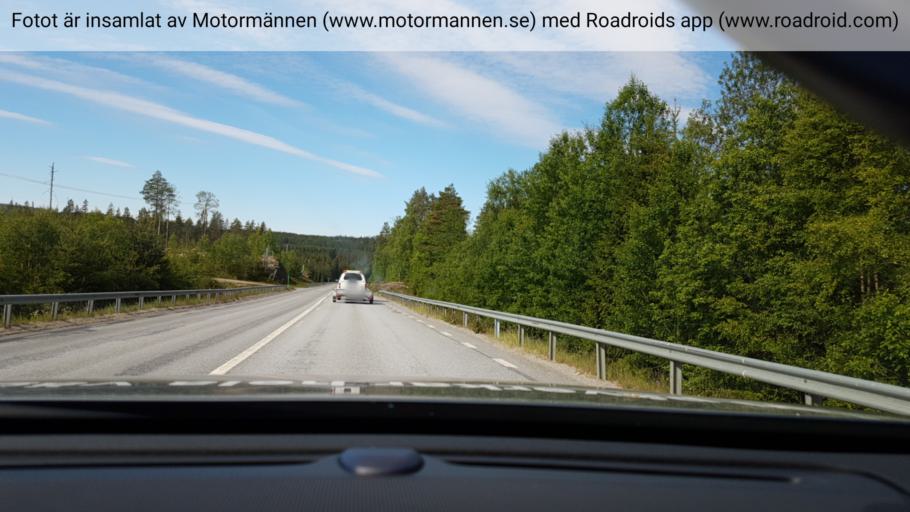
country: SE
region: Vaesterbotten
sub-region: Bjurholms Kommun
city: Bjurholm
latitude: 63.9332
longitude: 19.3084
